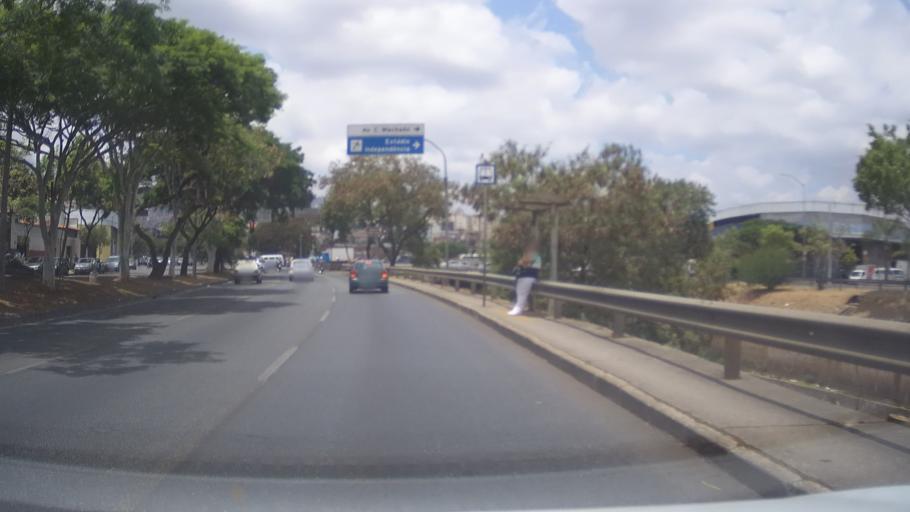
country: BR
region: Minas Gerais
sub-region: Belo Horizonte
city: Belo Horizonte
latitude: -19.9061
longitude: -43.9105
